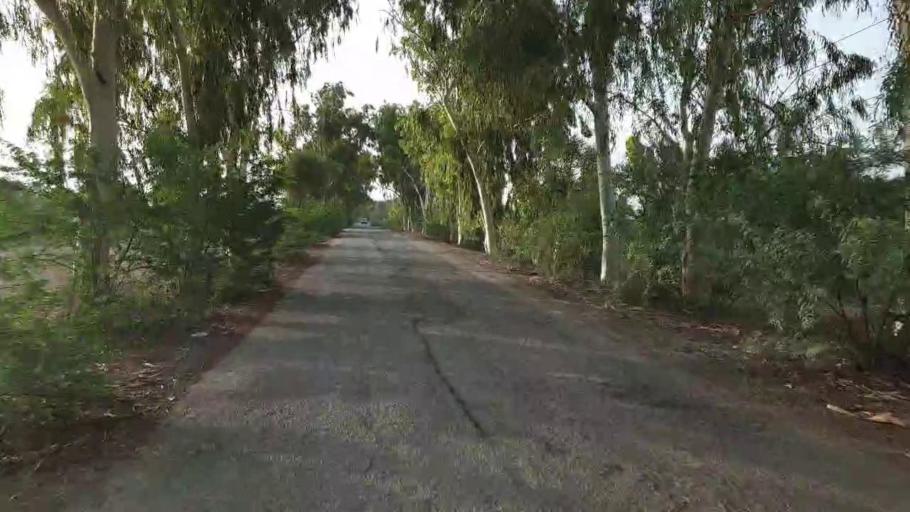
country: PK
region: Sindh
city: Bozdar
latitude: 27.1163
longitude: 68.9574
